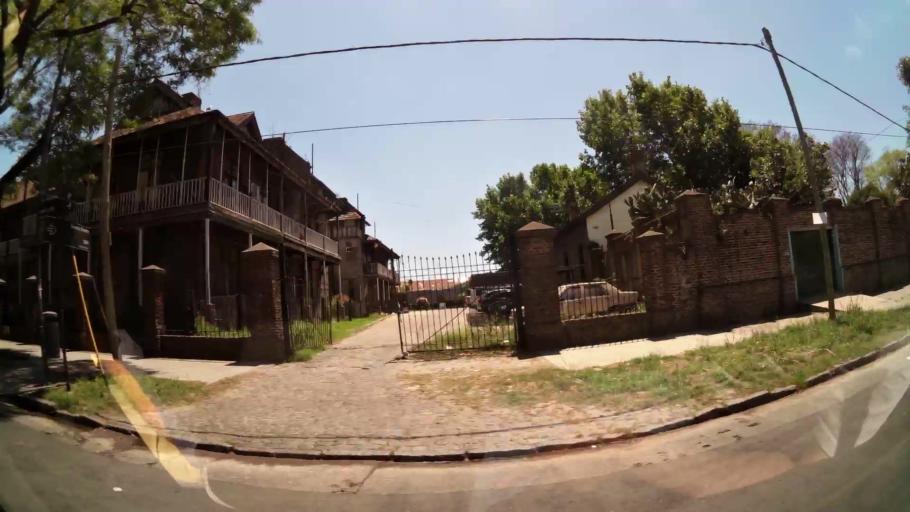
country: AR
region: Buenos Aires
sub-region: Partido de Avellaneda
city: Avellaneda
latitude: -34.6464
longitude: -58.3851
